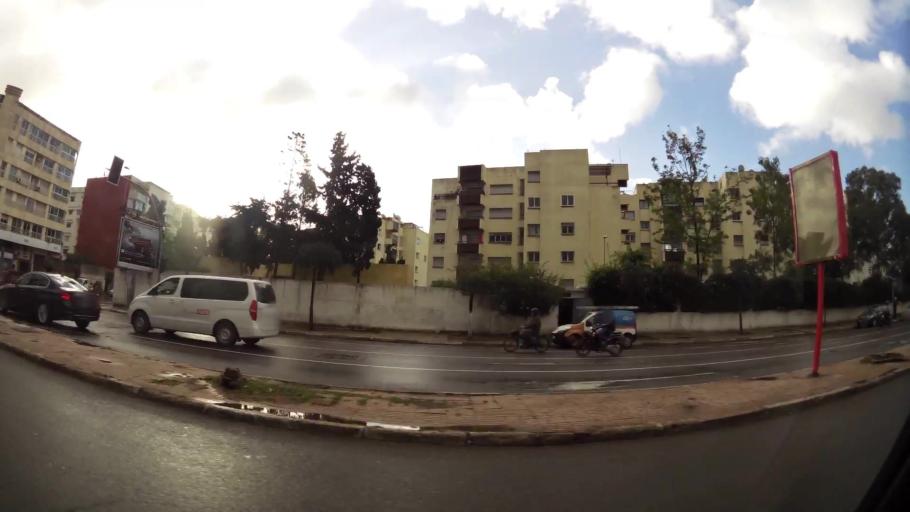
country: MA
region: Grand Casablanca
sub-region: Casablanca
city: Casablanca
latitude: 33.5733
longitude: -7.6409
